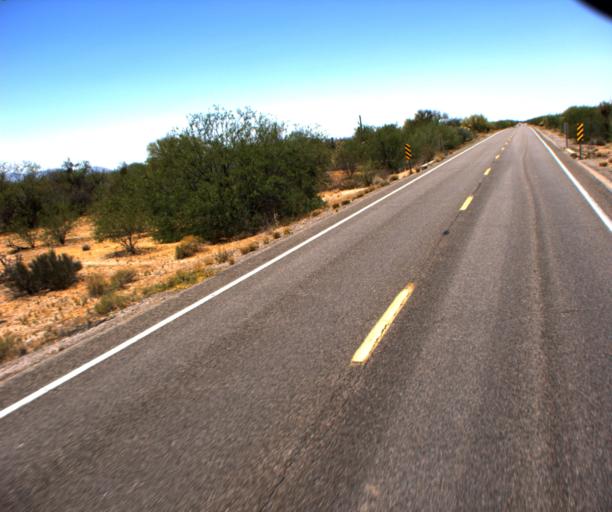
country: US
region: Arizona
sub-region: Pima County
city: Marana
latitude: 32.7552
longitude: -111.1393
